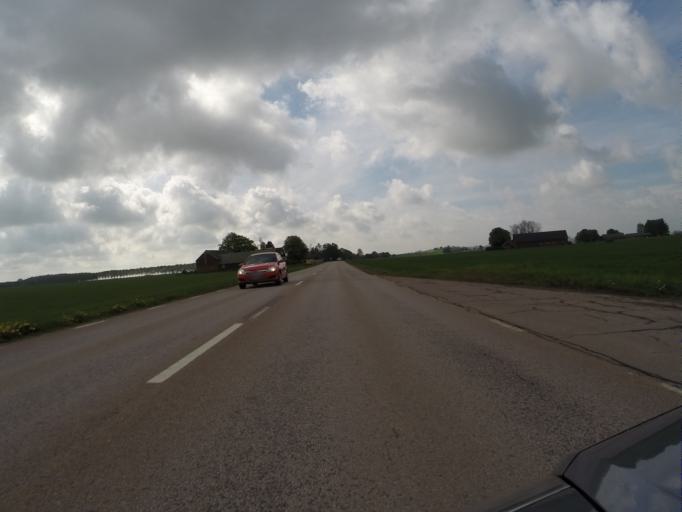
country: SE
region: Skane
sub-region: Landskrona
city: Asmundtorp
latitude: 55.9480
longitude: 12.9478
